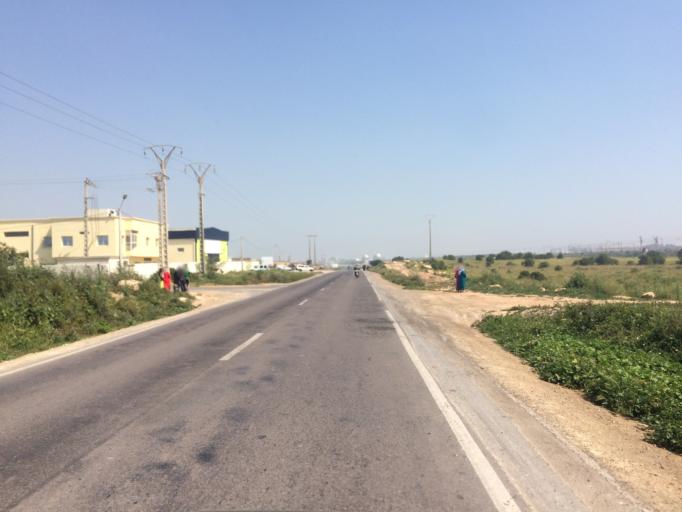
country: MA
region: Doukkala-Abda
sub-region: El-Jadida
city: Moulay Abdallah
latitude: 33.1508
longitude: -8.6056
